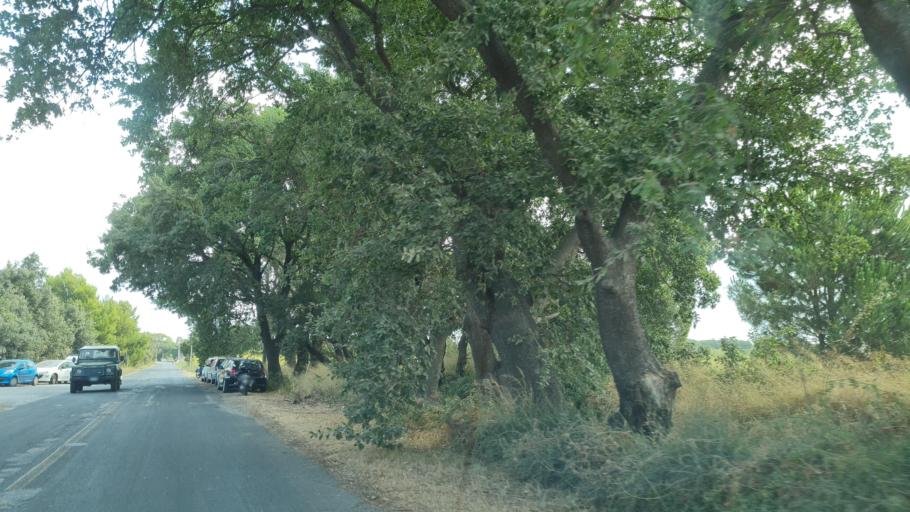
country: IT
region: Latium
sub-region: Provincia di Viterbo
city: Montalto di Castro
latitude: 42.3226
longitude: 11.6156
